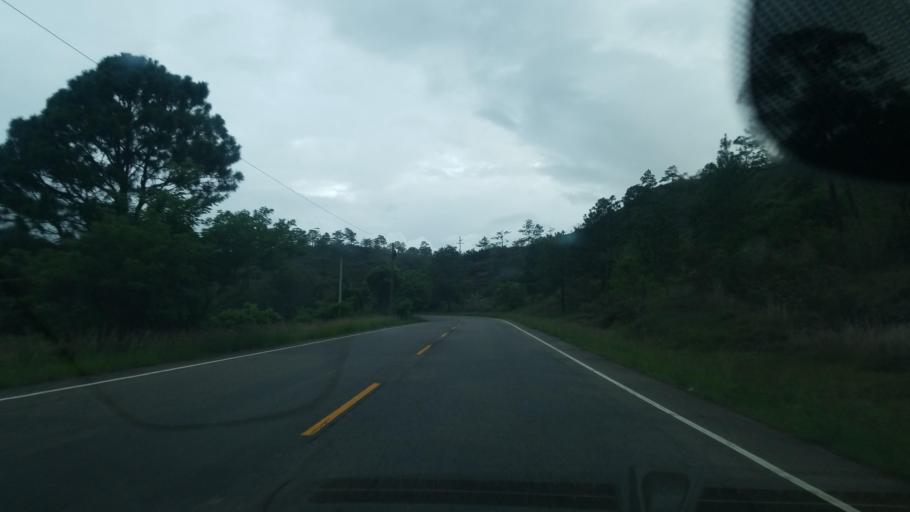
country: HN
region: Ocotepeque
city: Sinuapa
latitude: 14.5218
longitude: -89.2482
